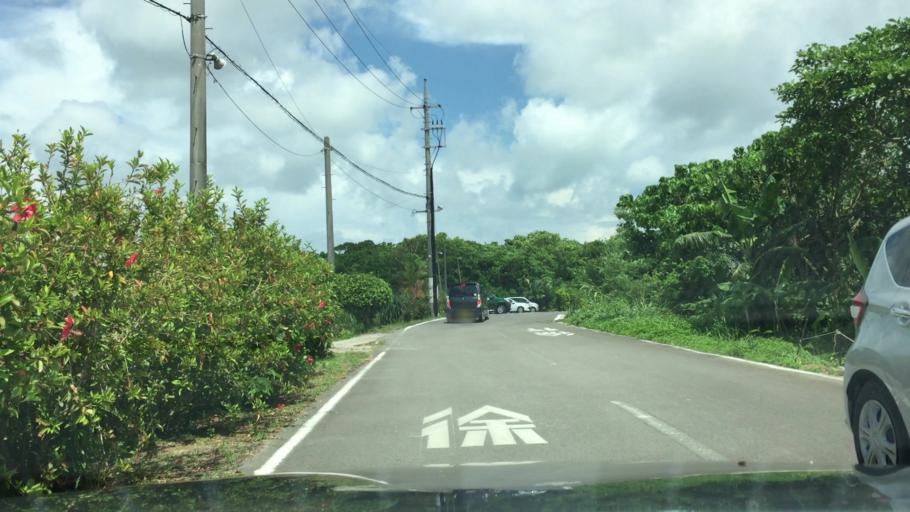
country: JP
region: Okinawa
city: Ishigaki
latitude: 24.3611
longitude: 124.1545
